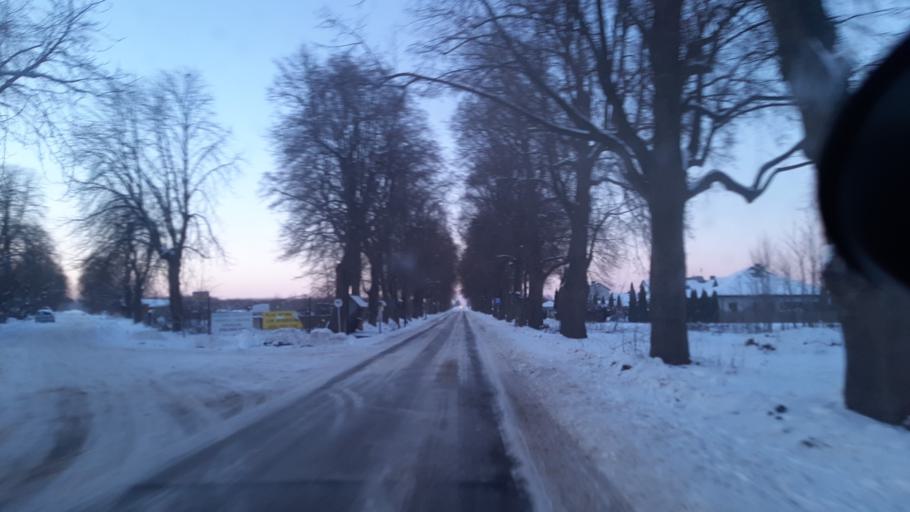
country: PL
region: Lublin Voivodeship
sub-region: Powiat lubelski
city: Lublin
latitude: 51.3331
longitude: 22.5539
